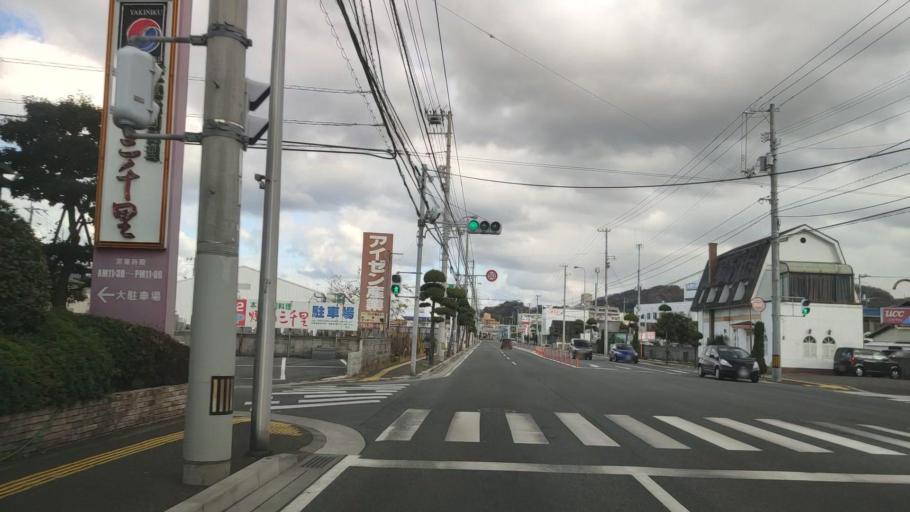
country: JP
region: Ehime
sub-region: Shikoku-chuo Shi
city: Matsuyama
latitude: 33.8667
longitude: 132.7512
